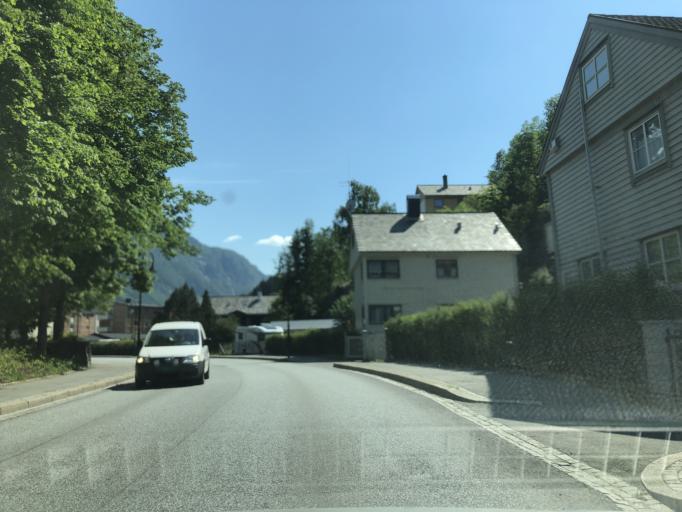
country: NO
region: Hordaland
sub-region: Odda
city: Odda
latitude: 60.0676
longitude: 6.5421
